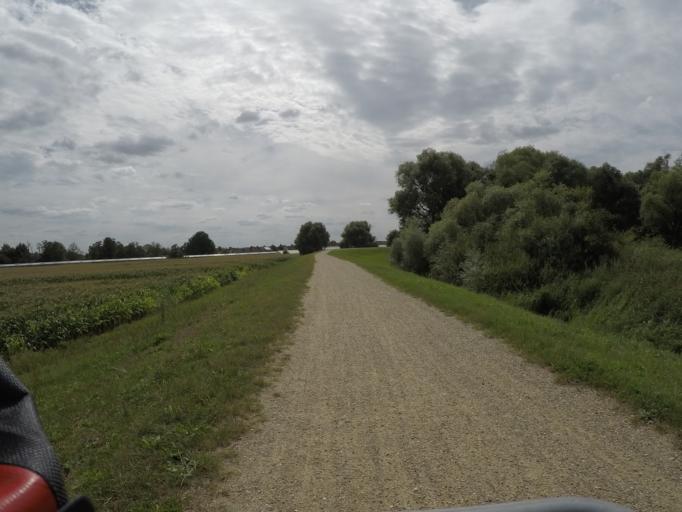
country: DE
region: Lower Saxony
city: Winsen
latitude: 53.3920
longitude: 10.1915
